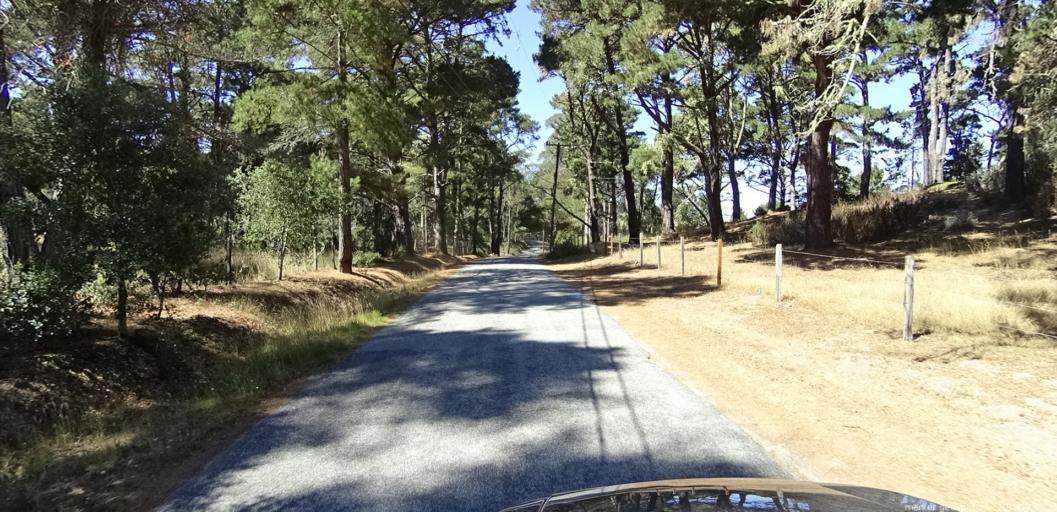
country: US
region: California
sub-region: Monterey County
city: Carmel-by-the-Sea
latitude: 36.5665
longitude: -121.8914
